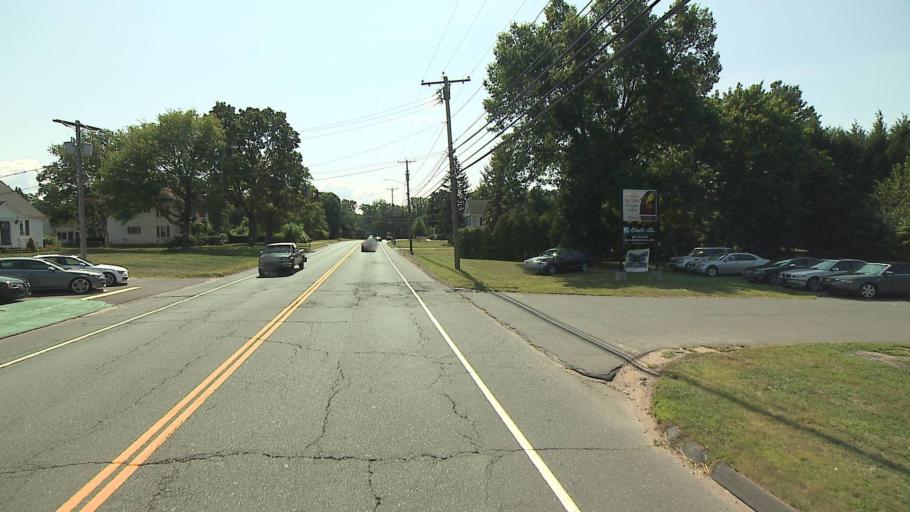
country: US
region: Connecticut
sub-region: Hartford County
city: Windsor Locks
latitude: 41.9008
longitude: -72.6099
